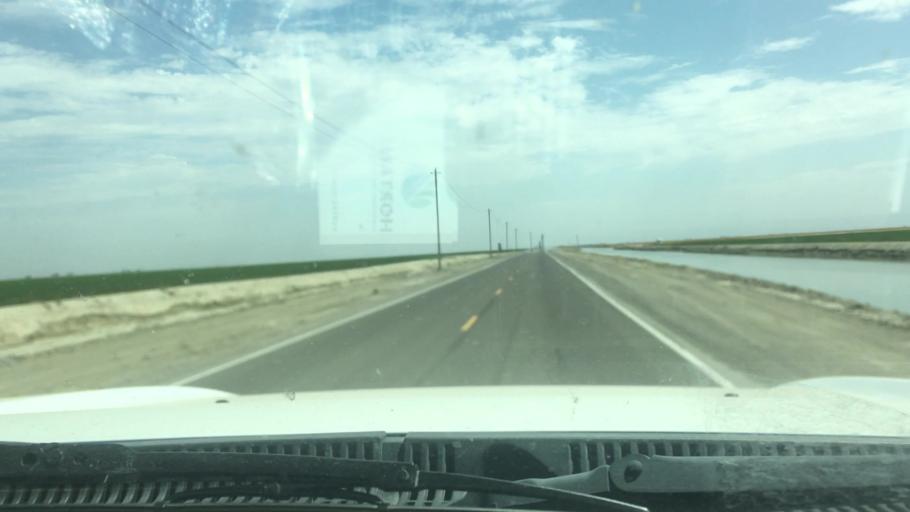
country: US
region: California
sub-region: Tulare County
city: Alpaugh
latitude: 35.8956
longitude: -119.5734
